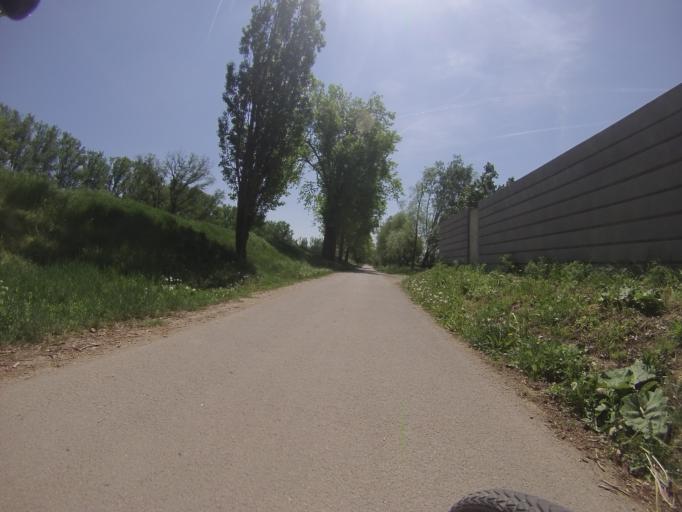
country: CZ
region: South Moravian
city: Zidlochovice
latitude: 49.0311
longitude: 16.6205
